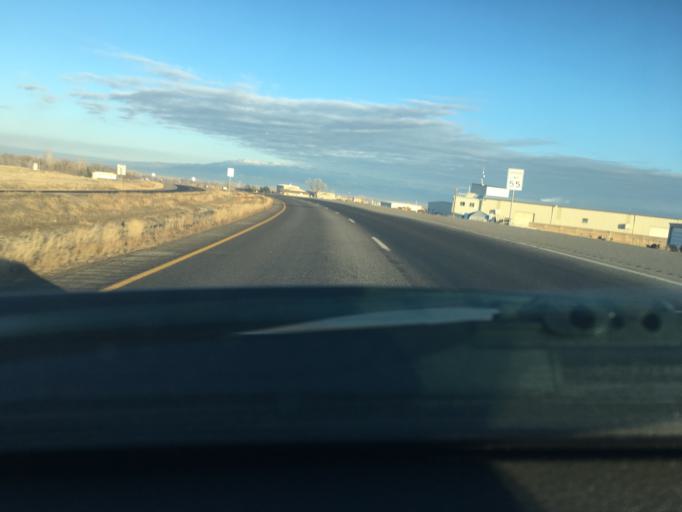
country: US
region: Colorado
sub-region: Montrose County
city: Olathe
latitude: 38.6080
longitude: -107.9739
